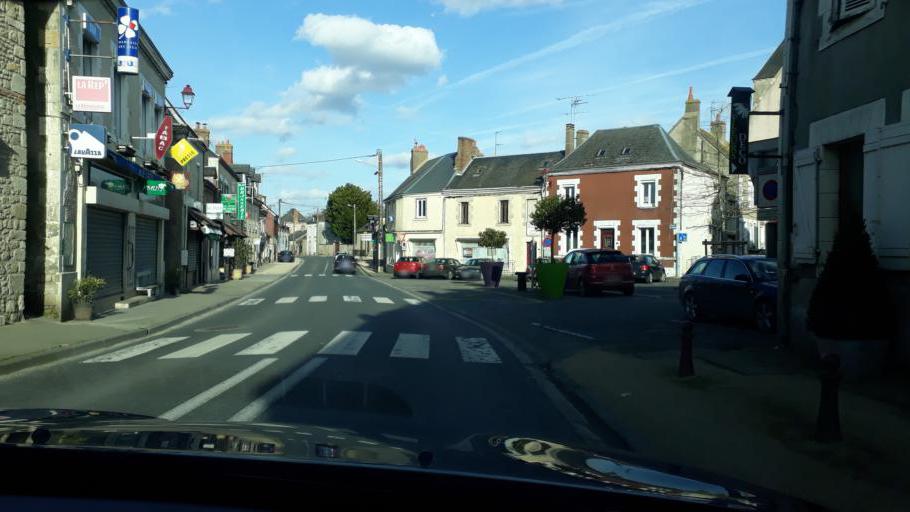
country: FR
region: Centre
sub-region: Departement du Loiret
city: Chilleurs-aux-Bois
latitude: 48.0717
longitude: 2.1345
